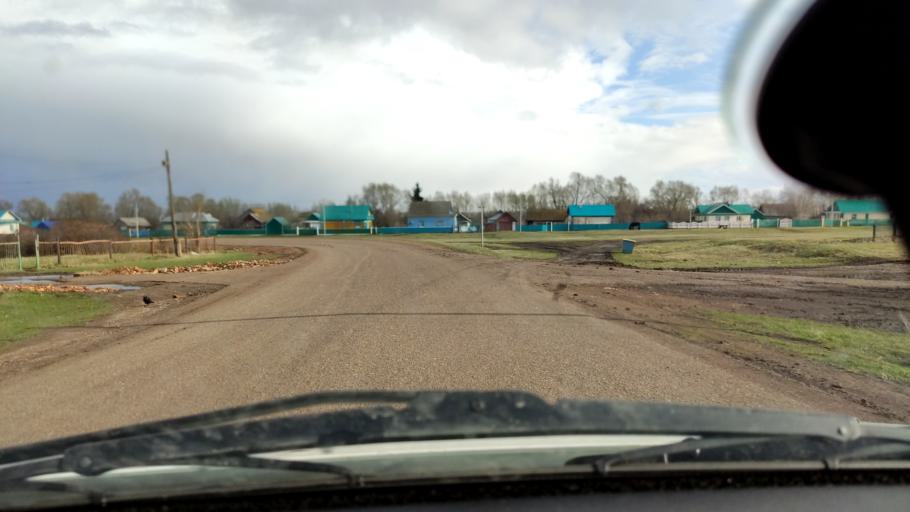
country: RU
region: Bashkortostan
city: Buzdyak
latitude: 54.7639
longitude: 54.6054
